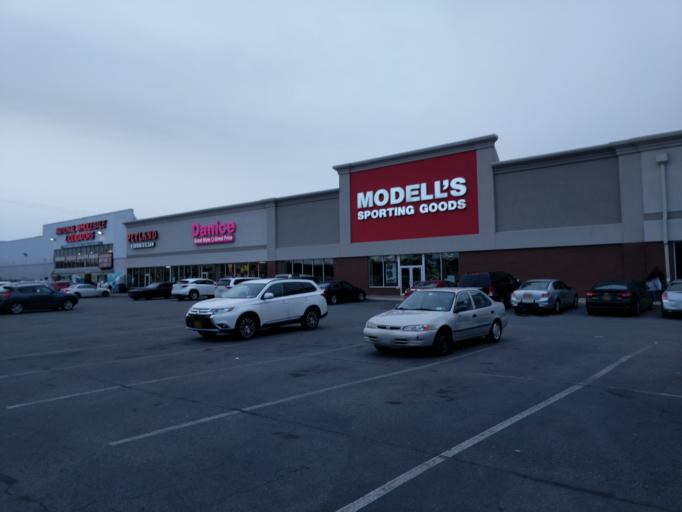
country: US
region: New York
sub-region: Queens County
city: Long Island City
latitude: 40.7527
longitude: -73.9166
